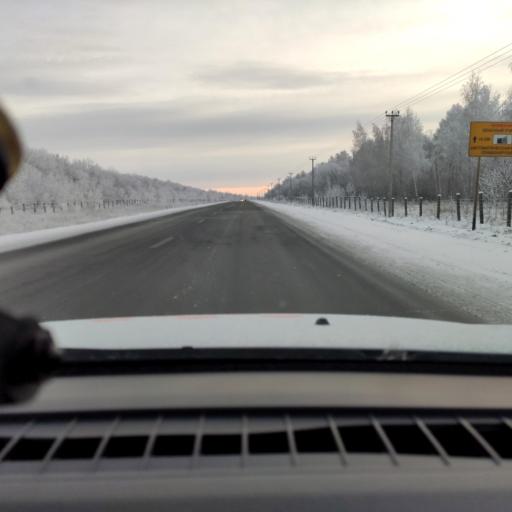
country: RU
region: Samara
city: Chapayevsk
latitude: 52.9966
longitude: 49.7938
